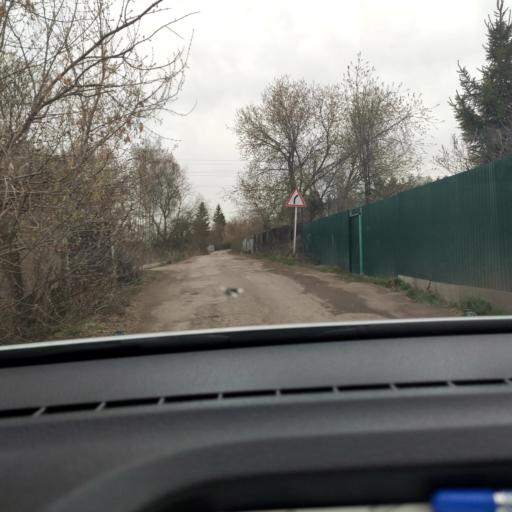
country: RU
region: Bashkortostan
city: Avdon
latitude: 54.6258
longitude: 55.5950
